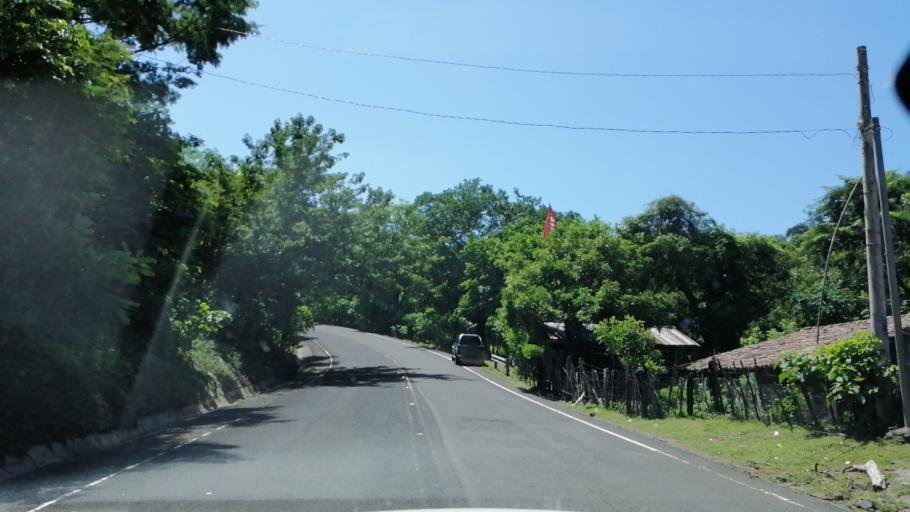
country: SV
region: San Miguel
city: Sesori
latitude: 13.8048
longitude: -88.3956
